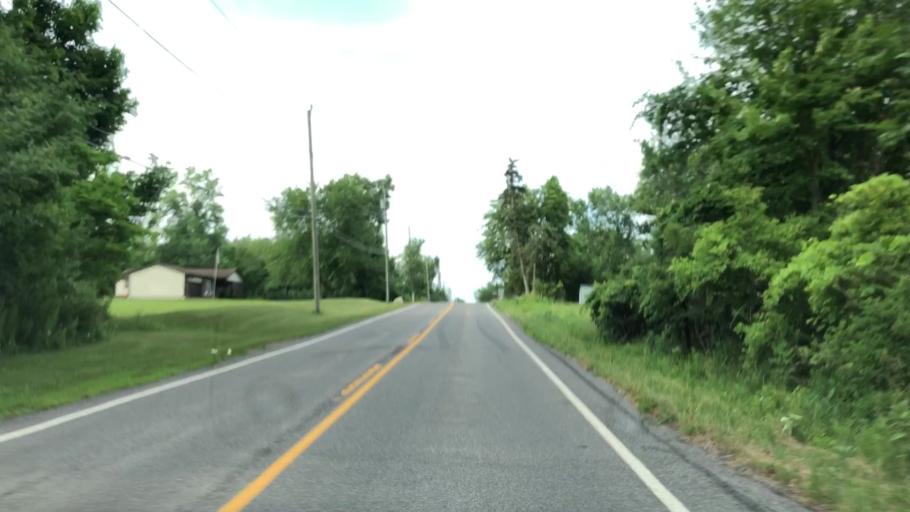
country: US
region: New York
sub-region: Erie County
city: Elma Center
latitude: 42.8441
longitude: -78.6923
